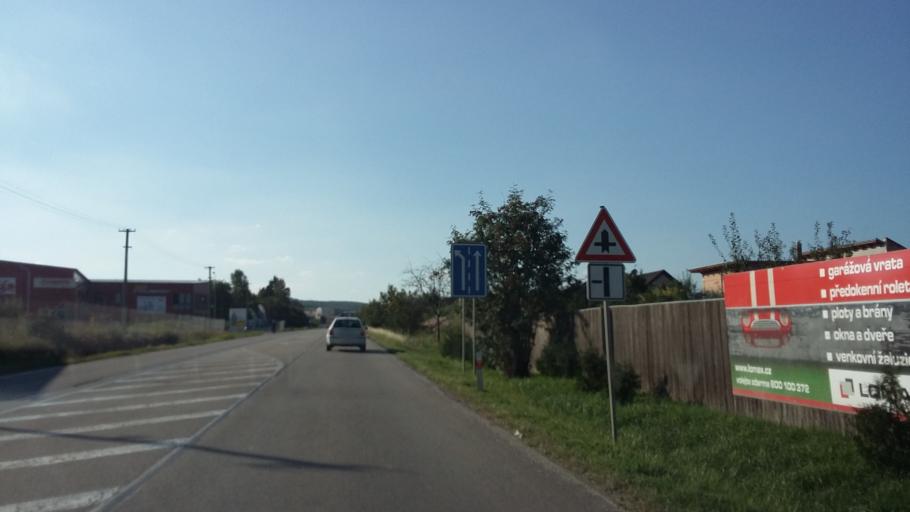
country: CZ
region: South Moravian
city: Troubsko
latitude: 49.1794
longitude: 16.4959
